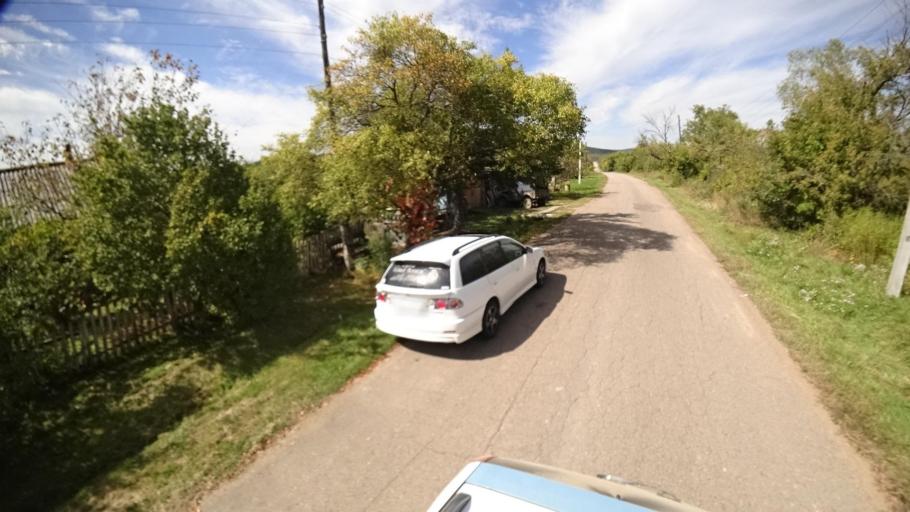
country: RU
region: Primorskiy
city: Yakovlevka
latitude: 44.6570
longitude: 133.7400
